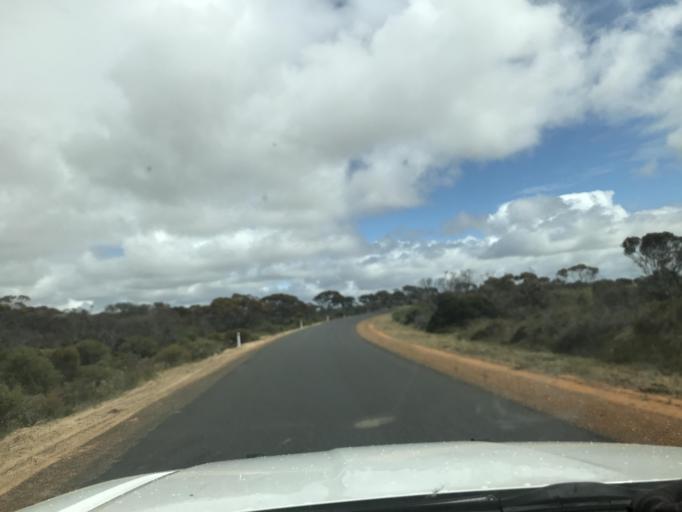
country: AU
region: South Australia
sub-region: Tatiara
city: Bordertown
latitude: -36.1768
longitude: 141.1538
